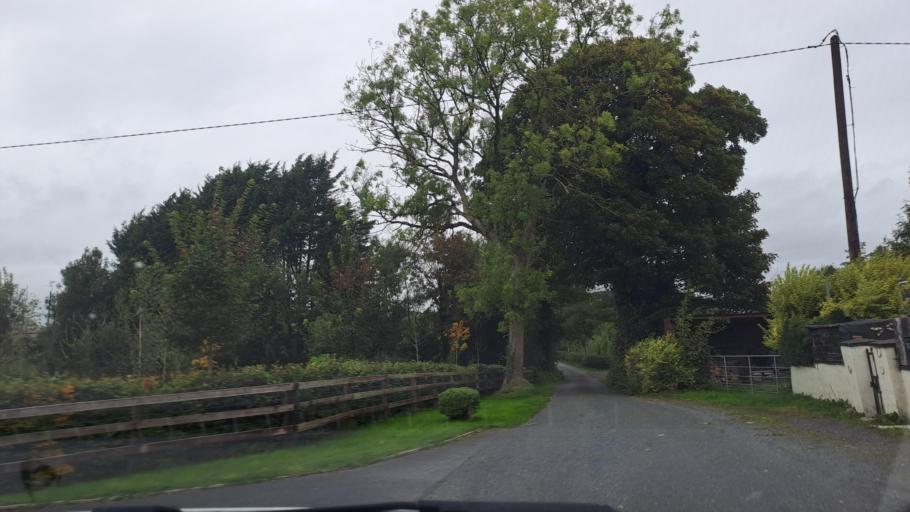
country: IE
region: Ulster
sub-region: County Monaghan
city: Carrickmacross
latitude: 53.9821
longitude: -6.7516
